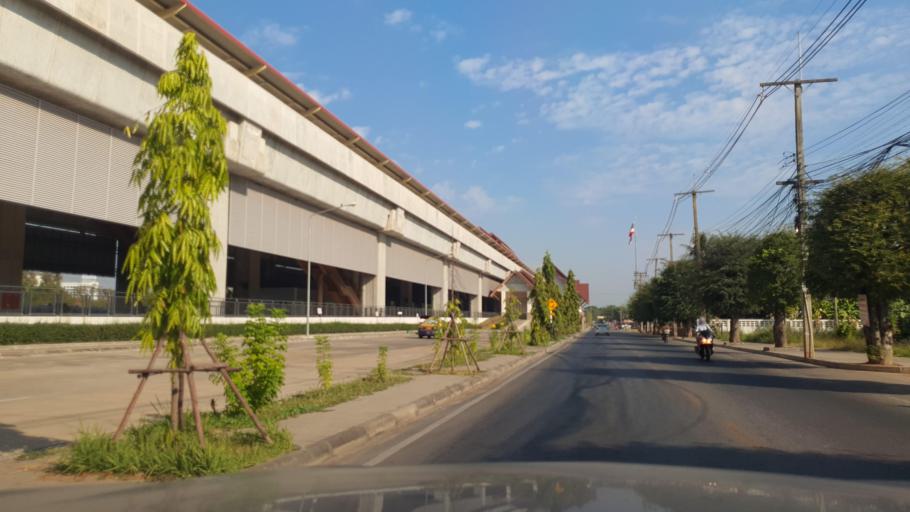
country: TH
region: Khon Kaen
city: Khon Kaen
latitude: 16.4250
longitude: 102.8255
